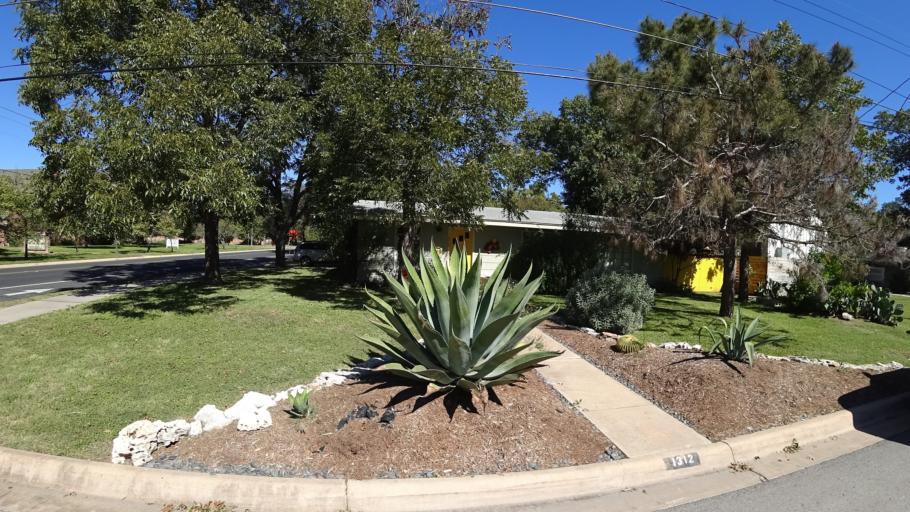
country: US
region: Texas
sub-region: Travis County
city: Austin
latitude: 30.3390
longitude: -97.7272
